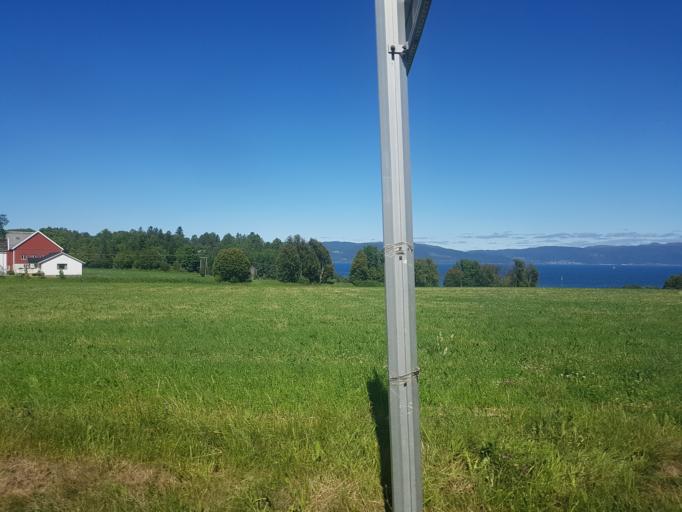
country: NO
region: Sor-Trondelag
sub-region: Skaun
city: Borsa
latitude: 63.4458
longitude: 10.1990
